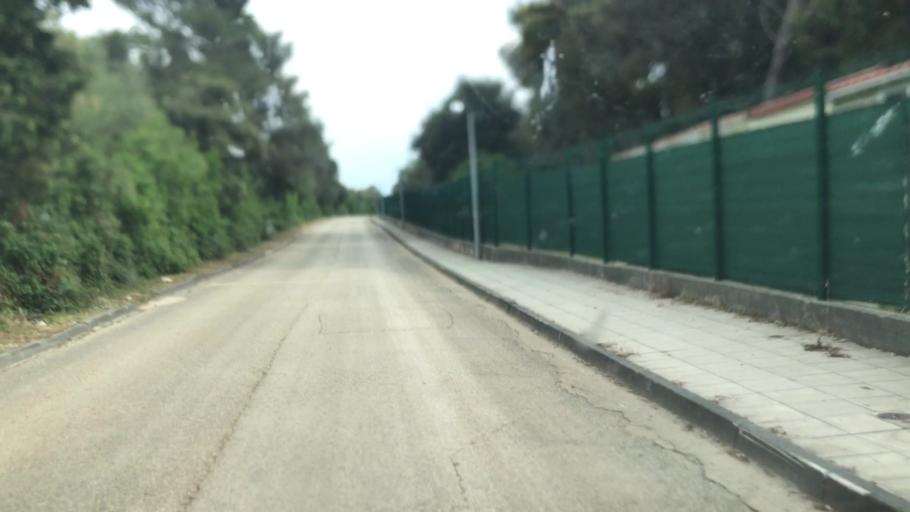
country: HR
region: Licko-Senjska
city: Novalja
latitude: 44.5446
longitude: 14.8818
